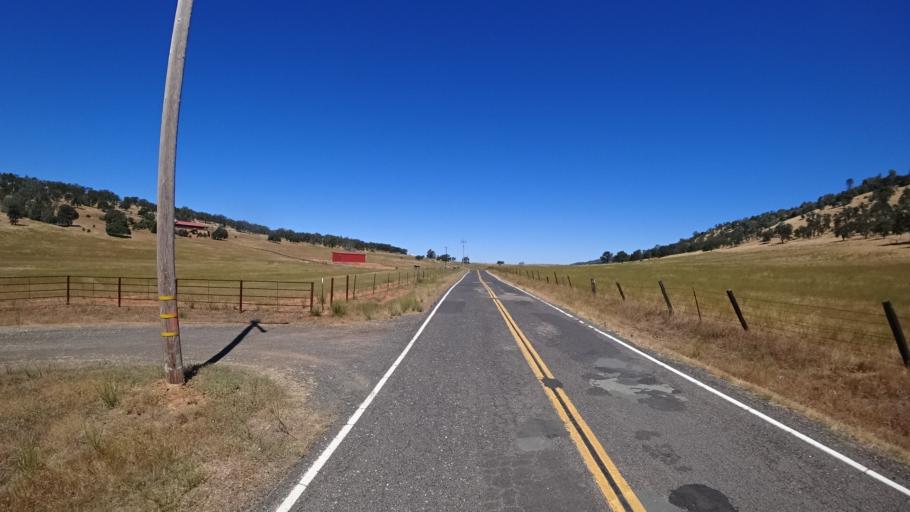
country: US
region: California
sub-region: Calaveras County
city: Copperopolis
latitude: 38.0206
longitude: -120.6826
